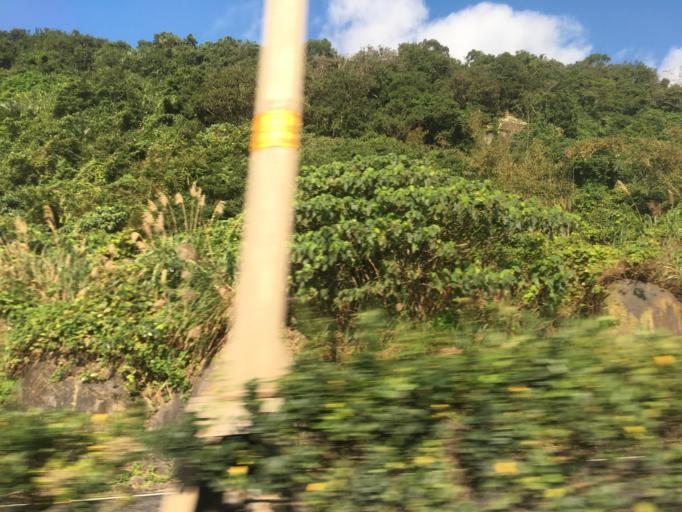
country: TW
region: Taiwan
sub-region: Yilan
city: Yilan
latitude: 24.8984
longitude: 121.8627
